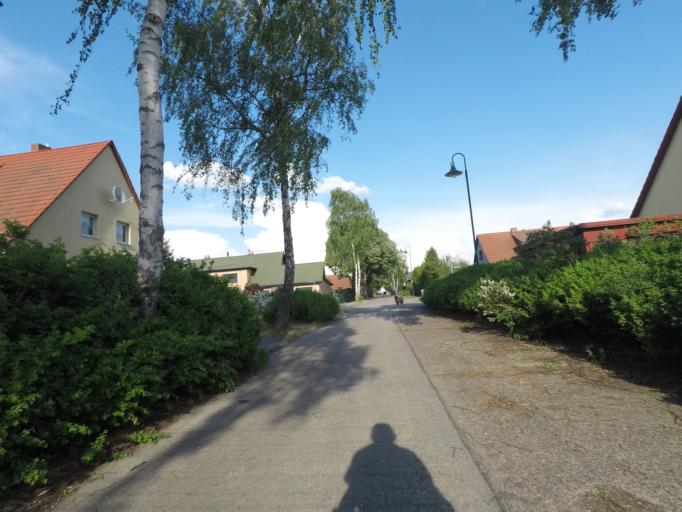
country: DE
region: Brandenburg
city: Melchow
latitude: 52.8336
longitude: 13.7208
